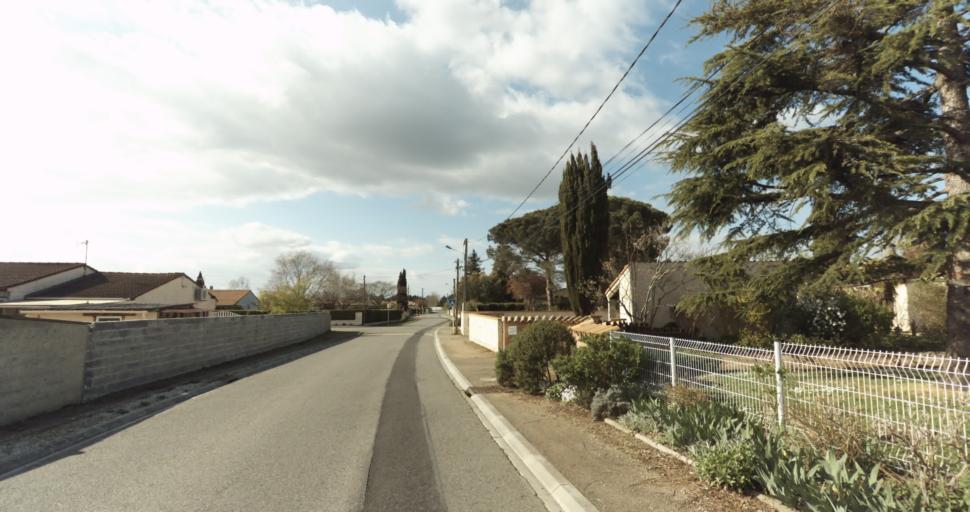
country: FR
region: Midi-Pyrenees
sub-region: Departement de la Haute-Garonne
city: Auterive
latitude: 43.3423
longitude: 1.4891
